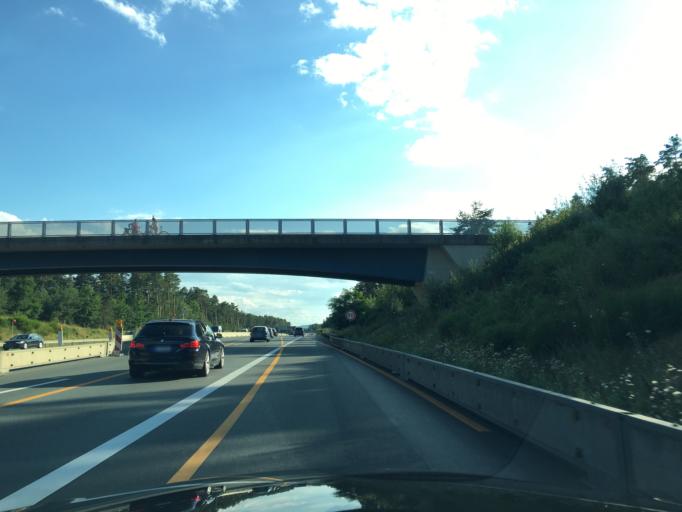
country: DE
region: Bavaria
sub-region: Regierungsbezirk Mittelfranken
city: Wendelstein
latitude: 49.3687
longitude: 11.1239
